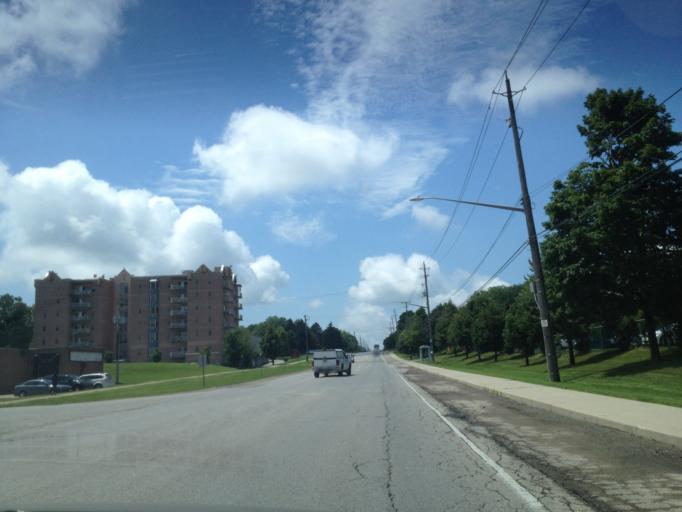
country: CA
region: Ontario
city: London
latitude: 43.0063
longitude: -81.3063
